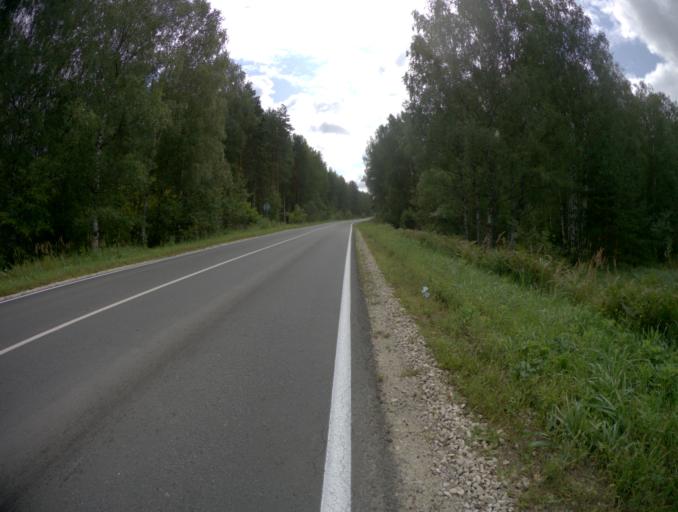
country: RU
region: Vladimir
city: Raduzhnyy
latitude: 55.9992
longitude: 40.2686
